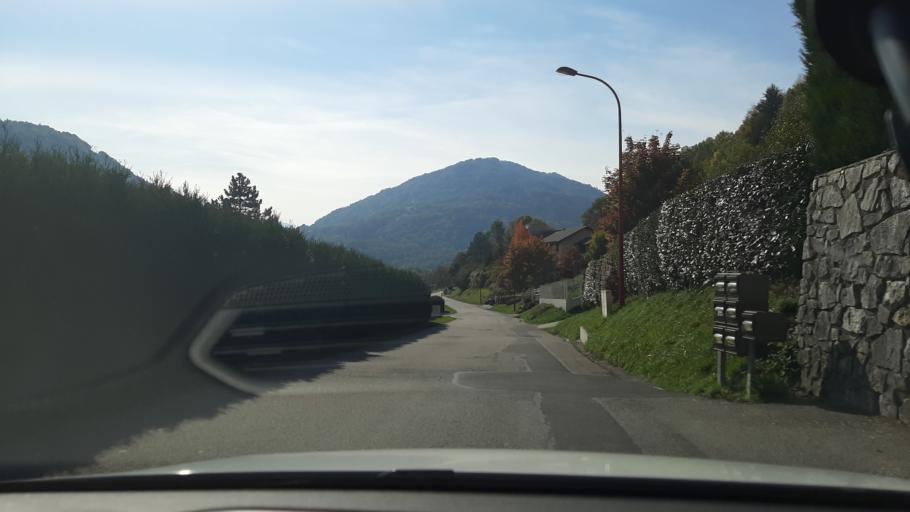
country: FR
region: Rhone-Alpes
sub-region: Departement de la Savoie
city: La Rochette
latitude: 45.4583
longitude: 6.1056
